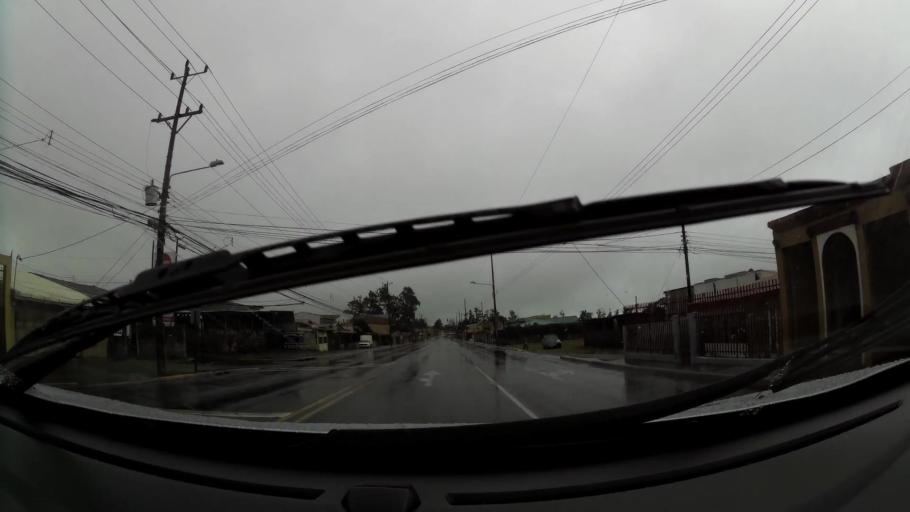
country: CR
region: Cartago
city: Cartago
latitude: 9.8617
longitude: -83.9112
